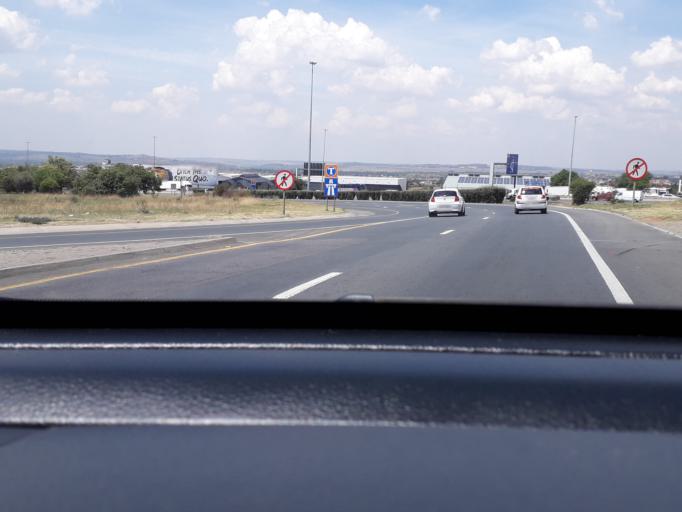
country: ZA
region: Gauteng
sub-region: City of Tshwane Metropolitan Municipality
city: Centurion
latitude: -25.9037
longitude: 28.1591
